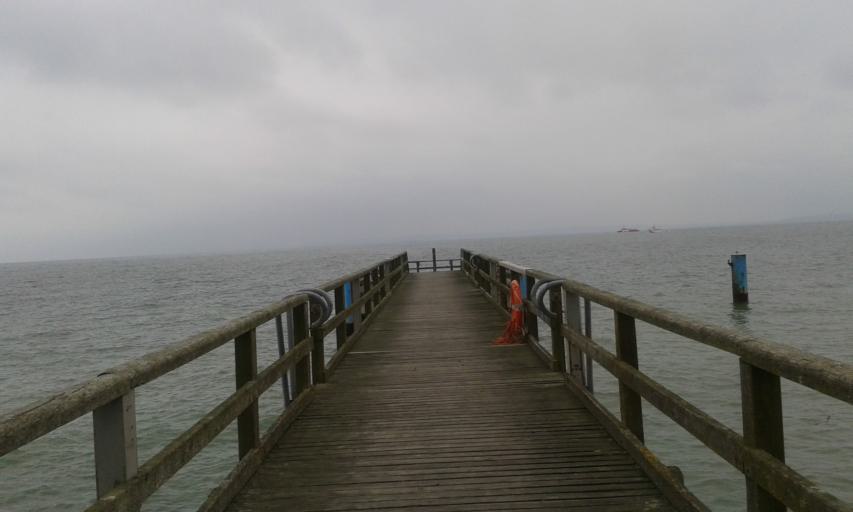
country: DE
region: Mecklenburg-Vorpommern
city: Sassnitz
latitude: 54.5162
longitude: 13.6559
